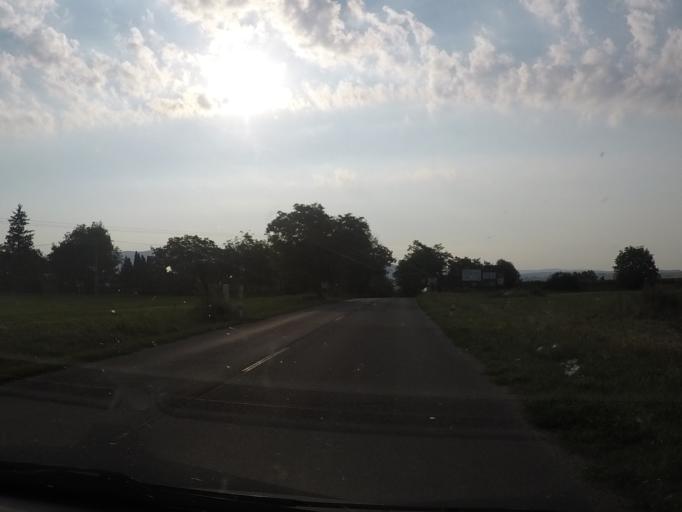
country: SK
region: Nitriansky
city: Zlate Moravce
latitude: 48.3879
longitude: 18.3684
